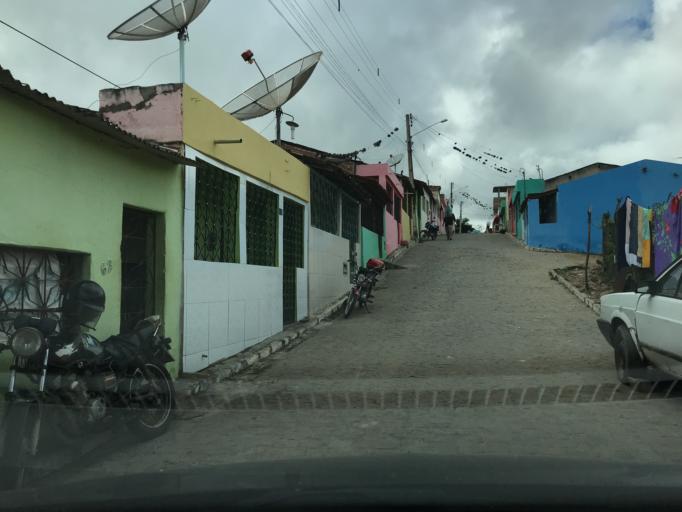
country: BR
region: Pernambuco
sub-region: Bezerros
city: Bezerros
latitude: -8.2311
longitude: -35.7613
